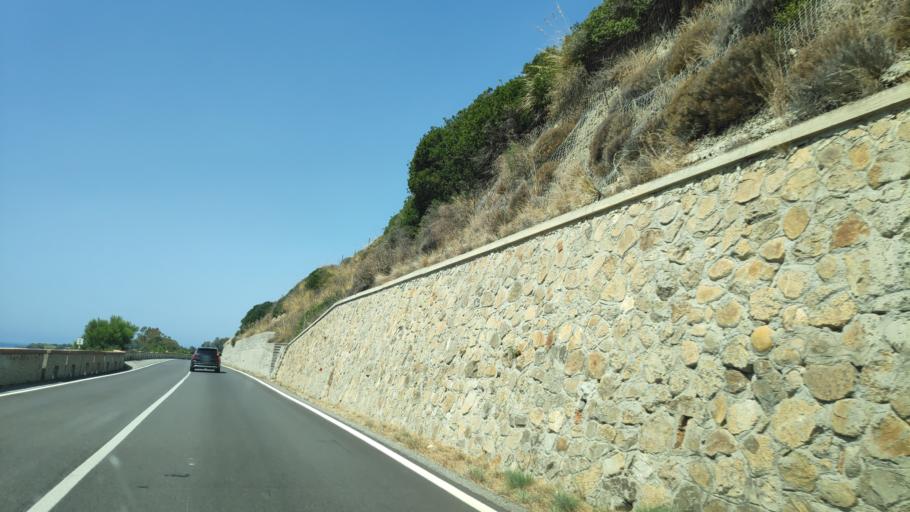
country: IT
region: Calabria
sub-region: Provincia di Reggio Calabria
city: Weather Station
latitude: 37.9250
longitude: 16.0575
